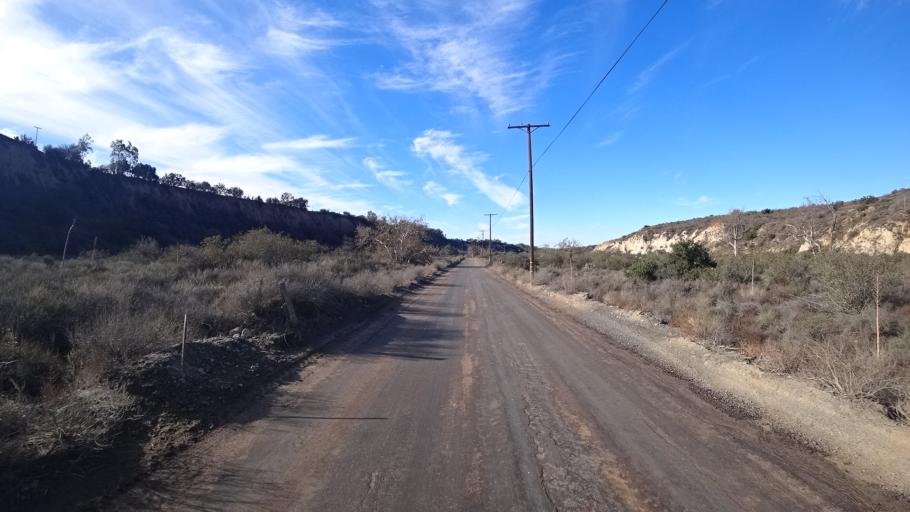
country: US
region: California
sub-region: Orange County
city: Trabuco Canyon
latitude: 33.6647
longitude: -117.5707
